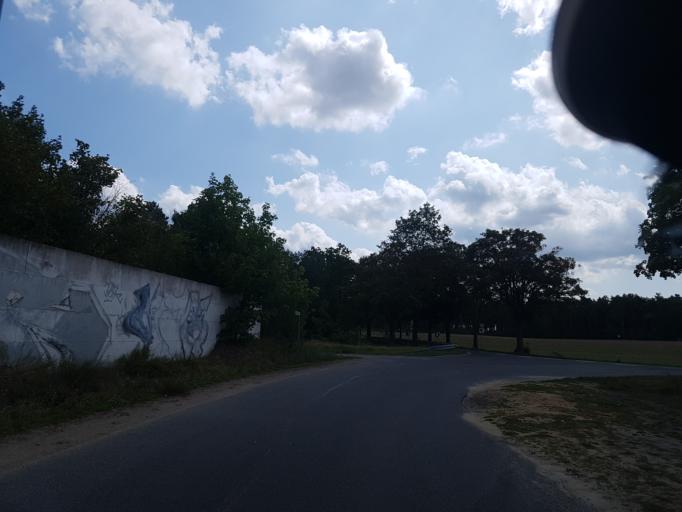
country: DE
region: Brandenburg
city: Borkwalde
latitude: 52.3026
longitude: 12.7955
